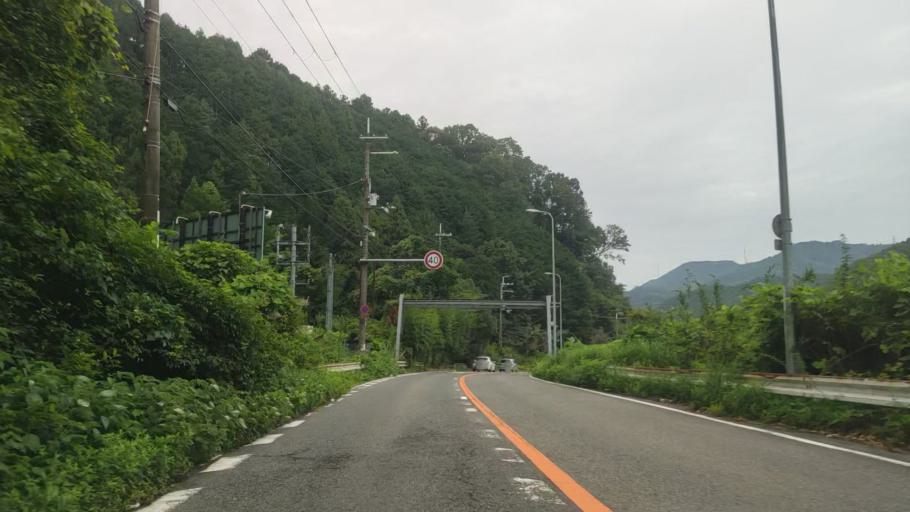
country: JP
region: Wakayama
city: Hashimoto
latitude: 34.3834
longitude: 135.6016
